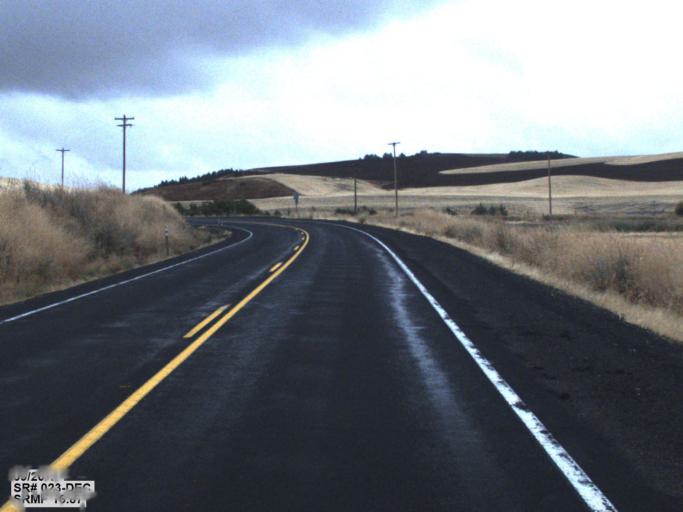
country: US
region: Washington
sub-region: Whitman County
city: Colfax
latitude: 47.1070
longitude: -117.6325
